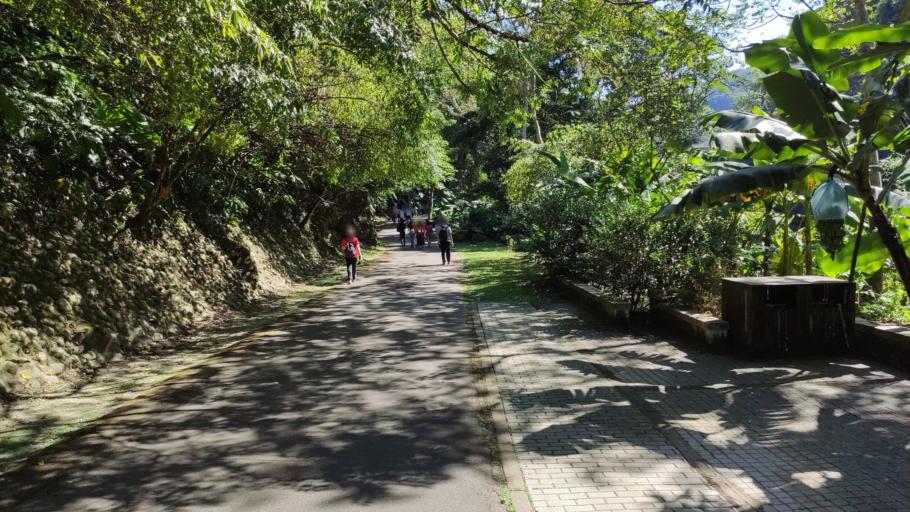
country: TW
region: Taiwan
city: Daxi
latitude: 24.8424
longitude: 121.3043
